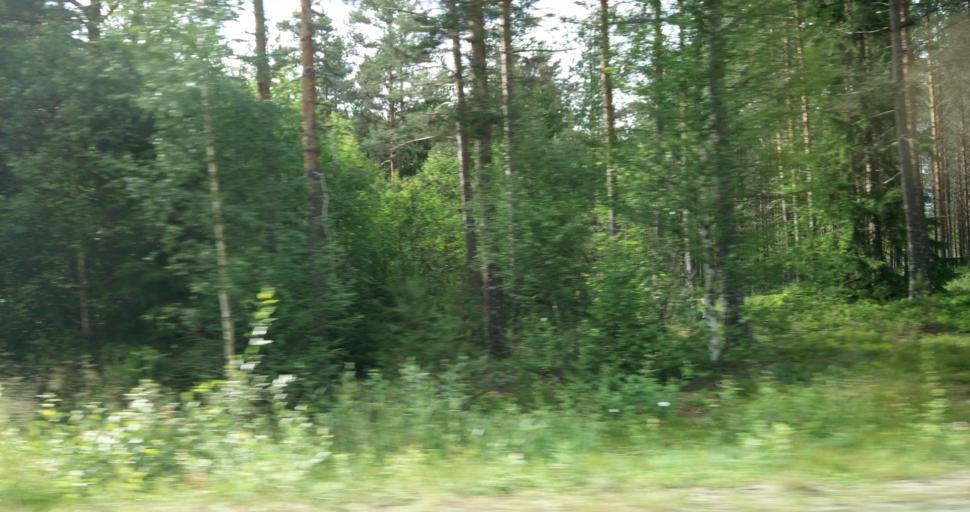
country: SE
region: Vaermland
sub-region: Hagfors Kommun
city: Ekshaerad
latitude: 60.0433
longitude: 13.5207
